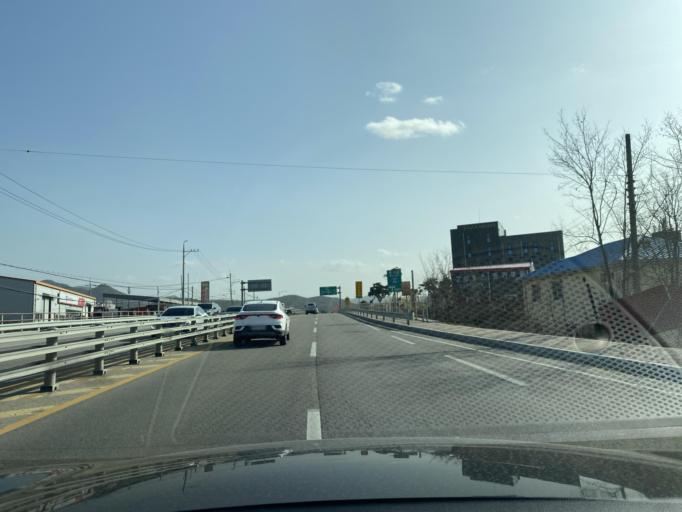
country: KR
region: Chungcheongnam-do
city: Yesan
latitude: 36.6847
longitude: 126.8175
